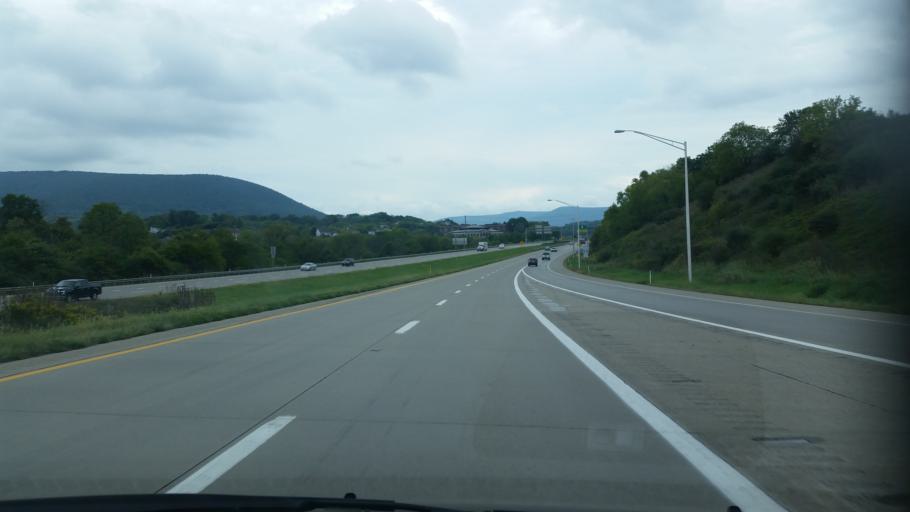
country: US
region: Pennsylvania
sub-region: Centre County
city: Houserville
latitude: 40.8208
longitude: -77.8373
